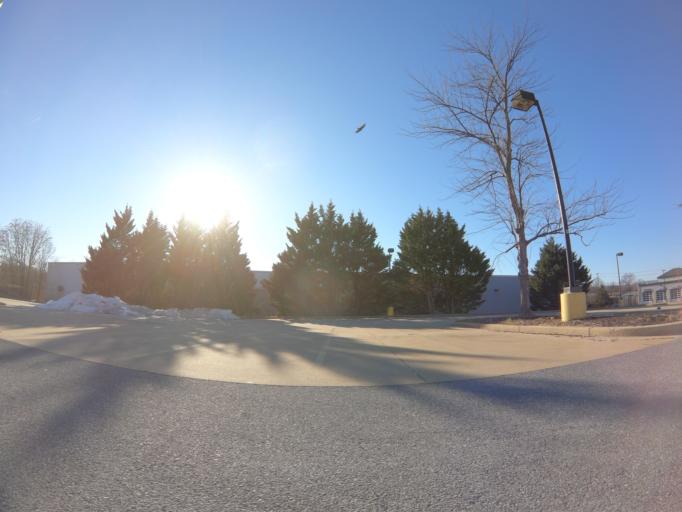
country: US
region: Maryland
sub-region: Frederick County
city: Frederick
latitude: 39.4458
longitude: -77.3881
